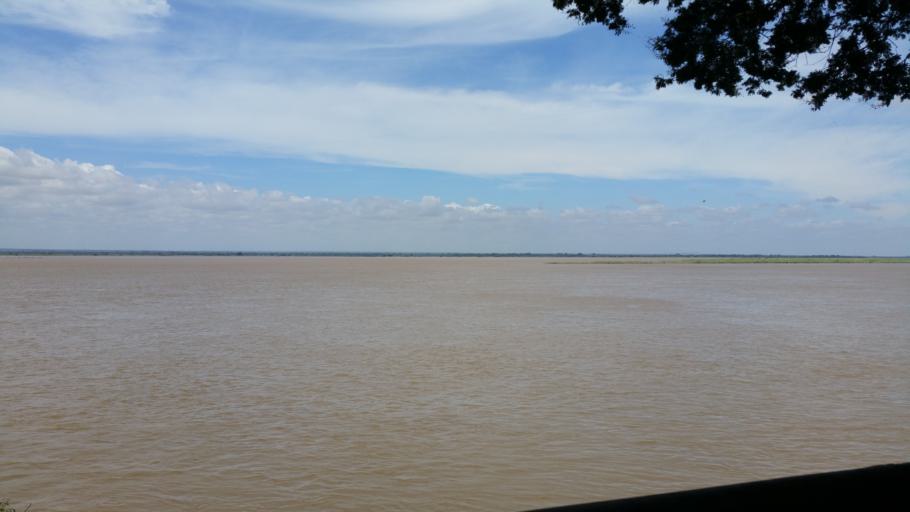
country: MM
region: Magway
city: Pakokku
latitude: 21.1837
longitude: 94.8672
